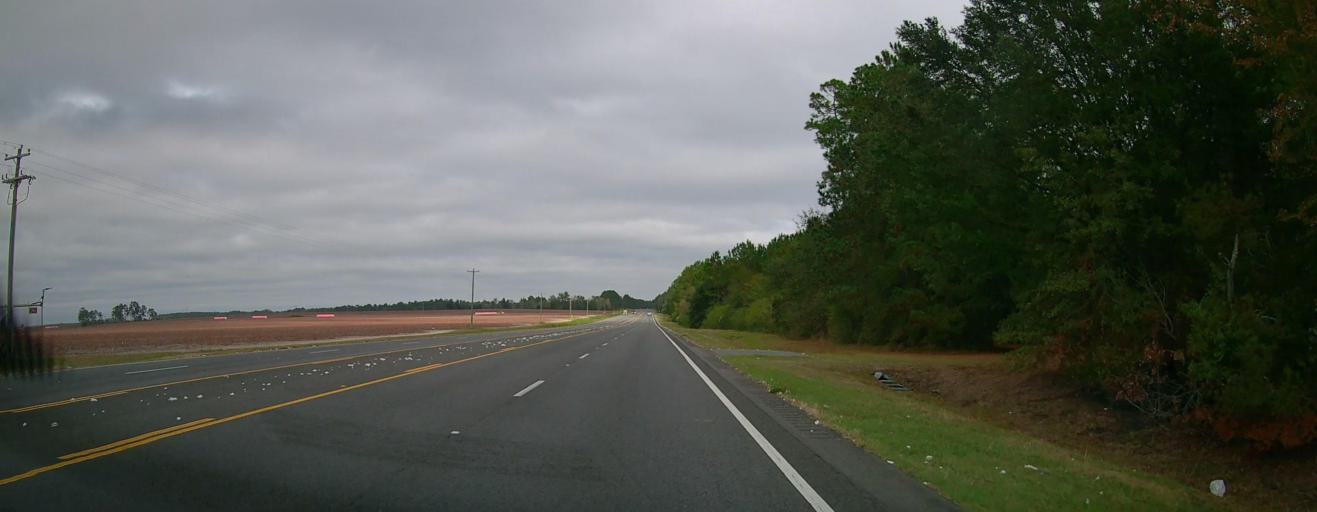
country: US
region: Georgia
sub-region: Colquitt County
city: Moultrie
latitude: 31.0278
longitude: -83.8610
